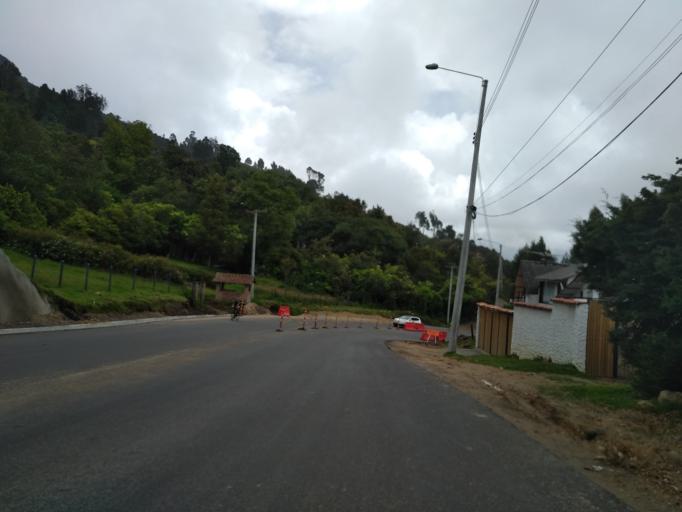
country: CO
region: Bogota D.C.
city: Barrio San Luis
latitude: 4.6695
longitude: -73.9978
